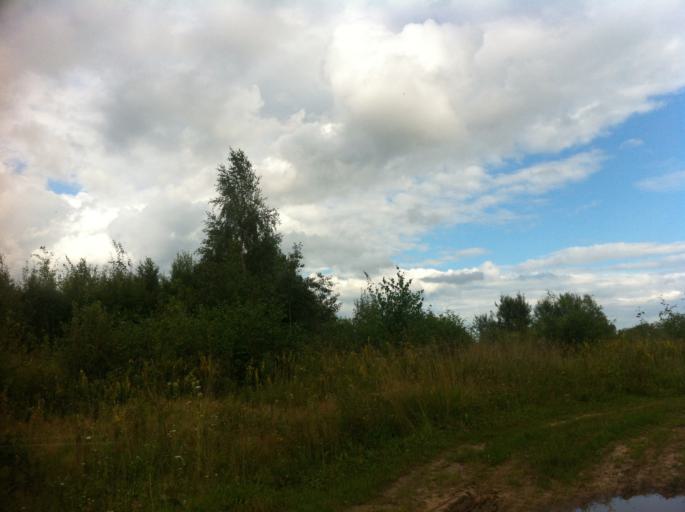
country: RU
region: Pskov
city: Izborsk
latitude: 57.8208
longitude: 27.9685
